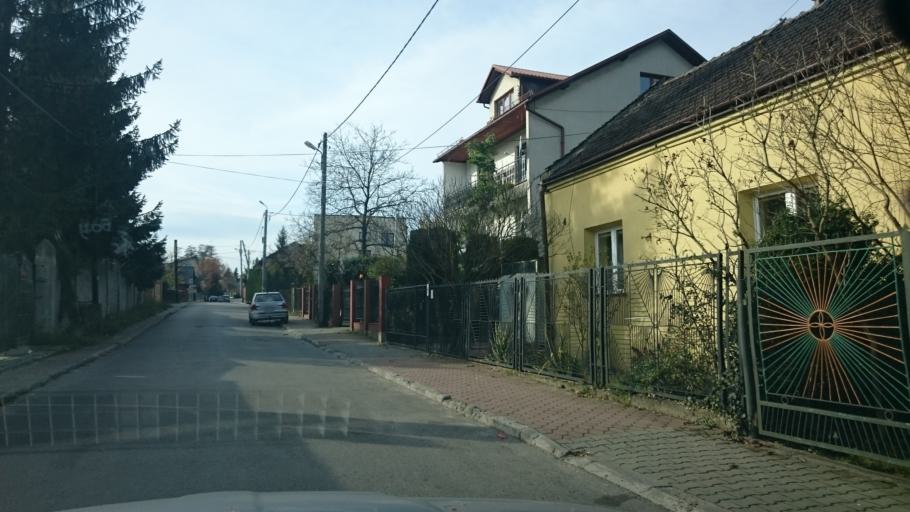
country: PL
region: Lesser Poland Voivodeship
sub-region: Krakow
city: Krakow
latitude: 50.0256
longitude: 19.9683
